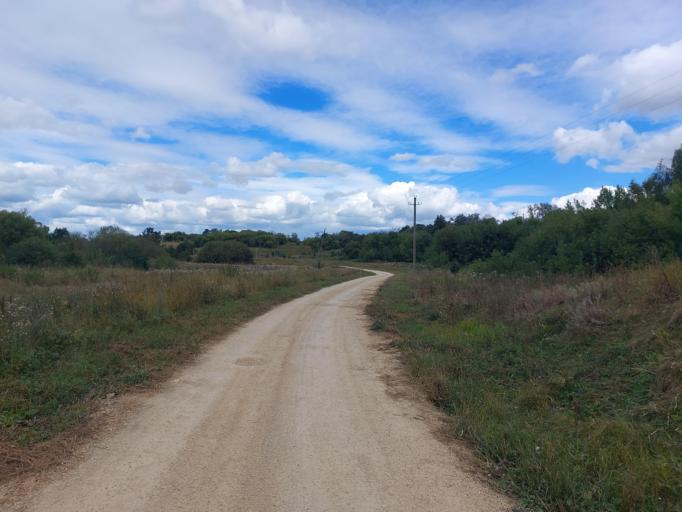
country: RU
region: Lipetsk
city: Terbuny
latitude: 52.2651
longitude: 38.2046
